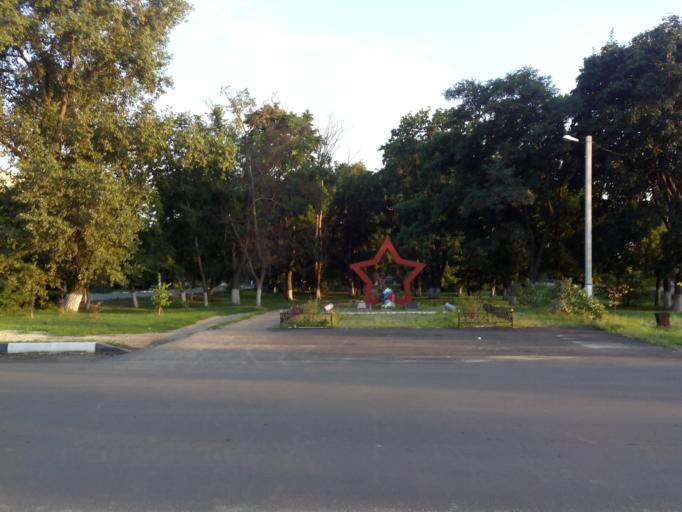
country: RU
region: Voronezj
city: Borisoglebsk
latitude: 51.3620
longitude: 42.0758
